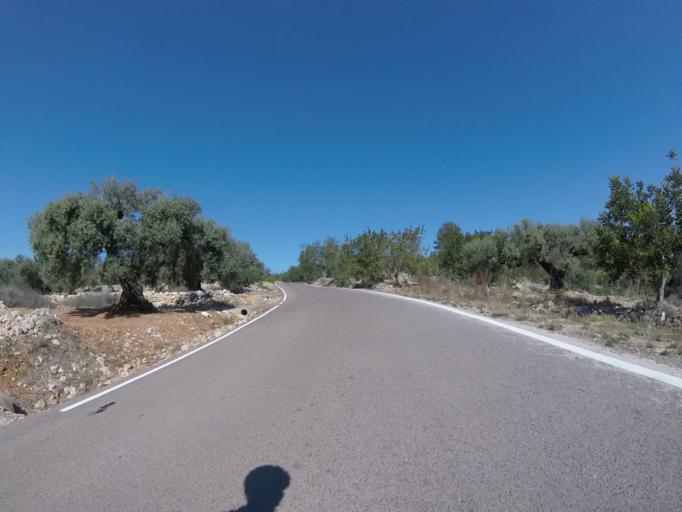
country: ES
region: Valencia
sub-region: Provincia de Castello
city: Santa Magdalena de Pulpis
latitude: 40.3736
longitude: 0.2724
